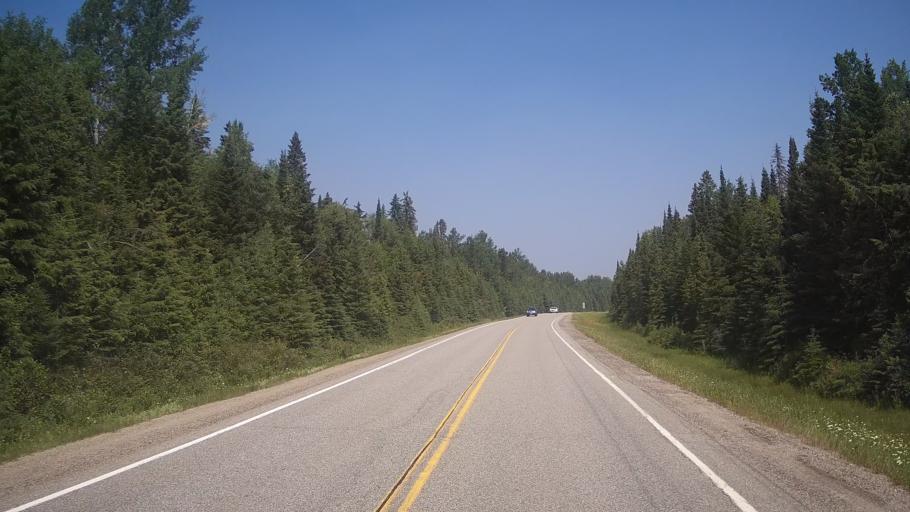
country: CA
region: Ontario
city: Timmins
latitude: 48.0796
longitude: -81.5962
